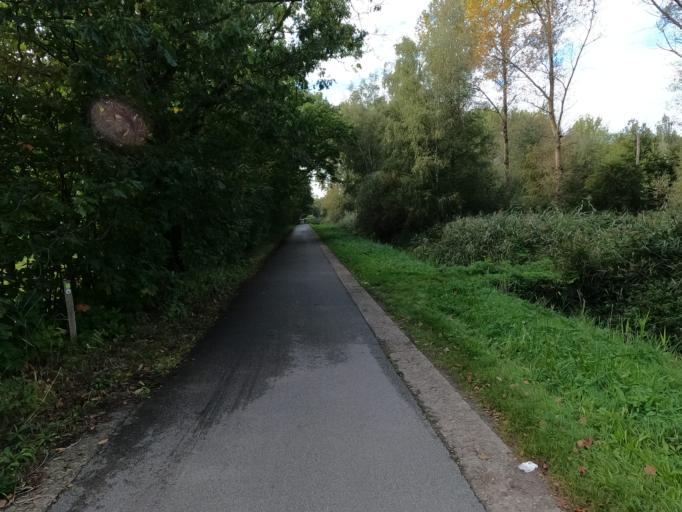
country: BE
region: Flanders
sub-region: Provincie Antwerpen
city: Herentals
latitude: 51.1815
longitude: 4.8004
